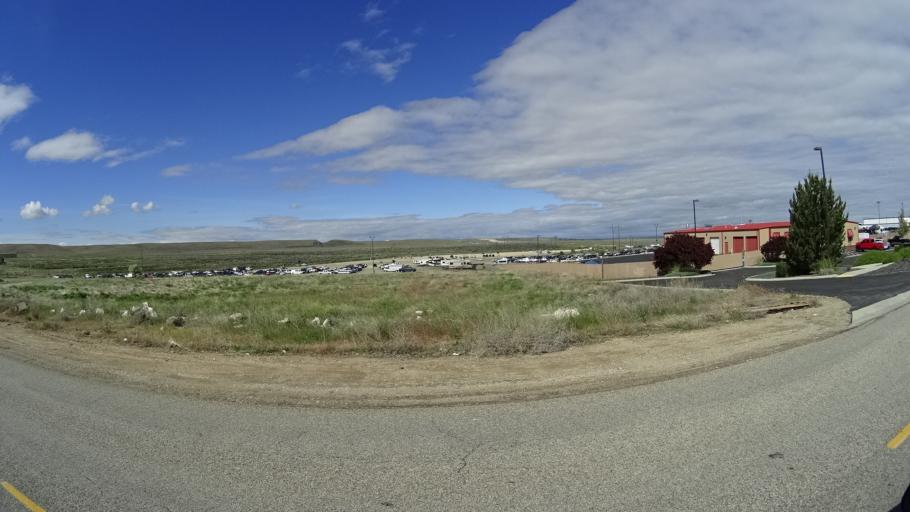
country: US
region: Idaho
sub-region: Ada County
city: Boise
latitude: 43.5335
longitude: -116.1595
